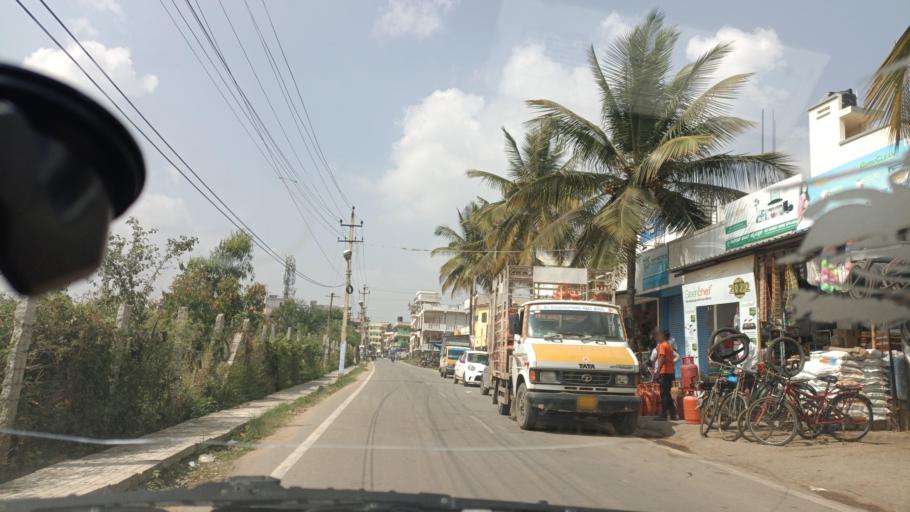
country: IN
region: Karnataka
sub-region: Bangalore Urban
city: Yelahanka
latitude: 13.1430
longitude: 77.6229
